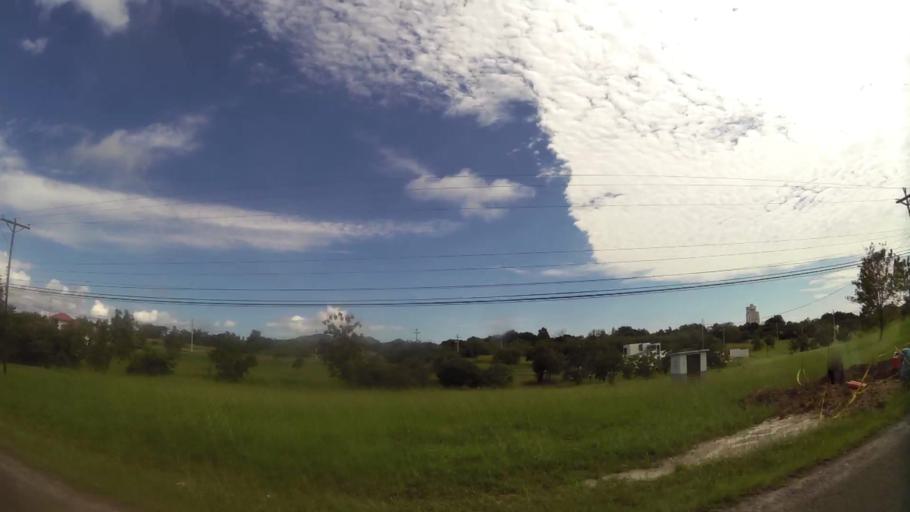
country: PA
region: Panama
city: Nueva Gorgona
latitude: 8.5407
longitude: -79.8990
